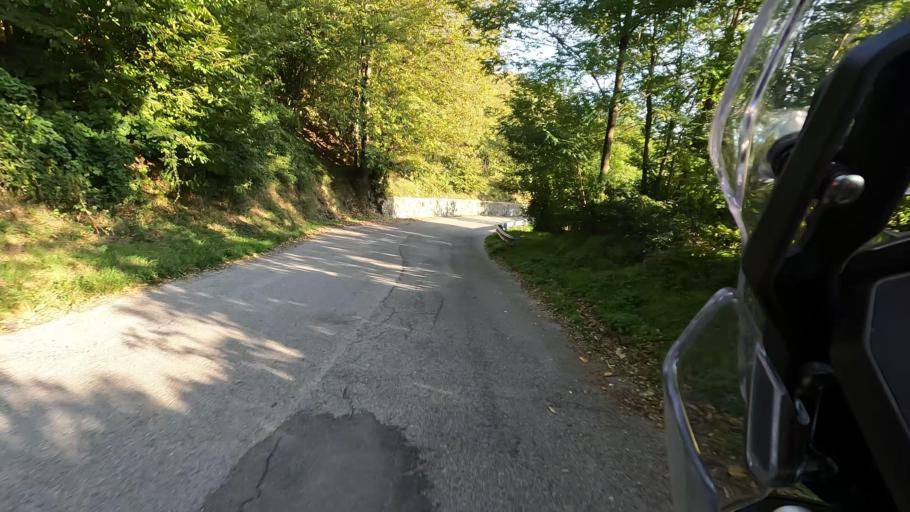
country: IT
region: Liguria
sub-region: Provincia di Savona
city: San Giovanni
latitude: 44.4107
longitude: 8.5192
